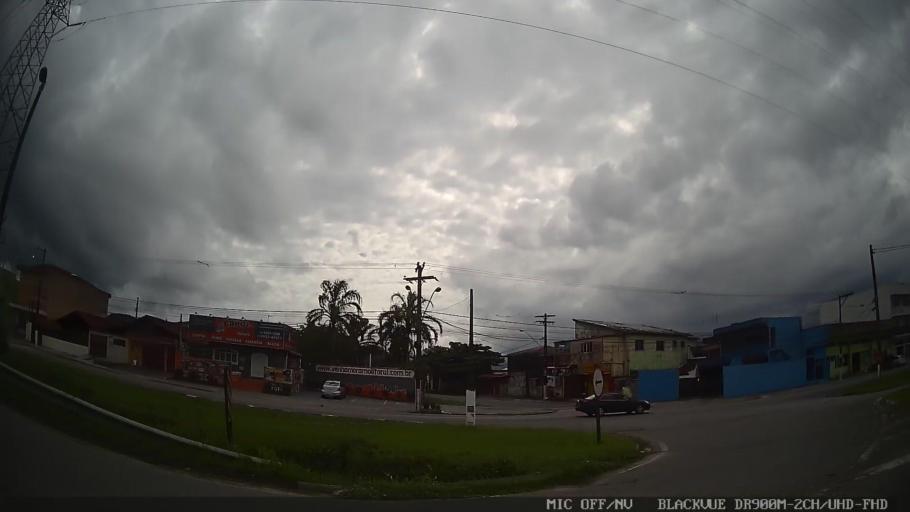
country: BR
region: Sao Paulo
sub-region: Mongagua
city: Mongagua
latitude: -24.1146
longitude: -46.6631
